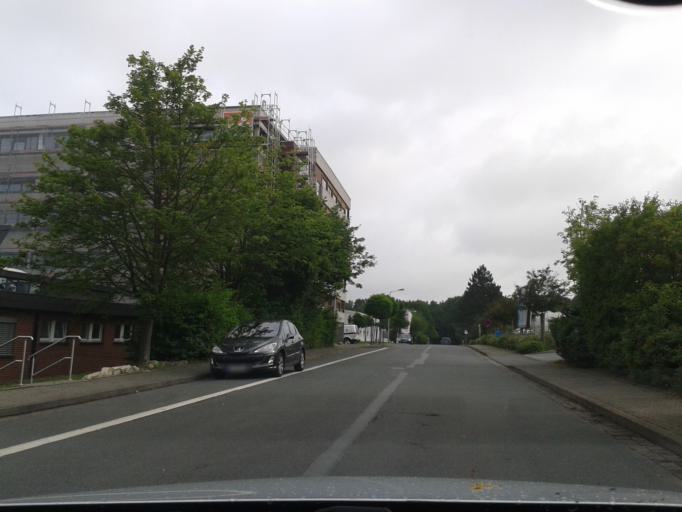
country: DE
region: North Rhine-Westphalia
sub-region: Regierungsbezirk Detmold
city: Barntrup
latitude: 51.9859
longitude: 9.1334
